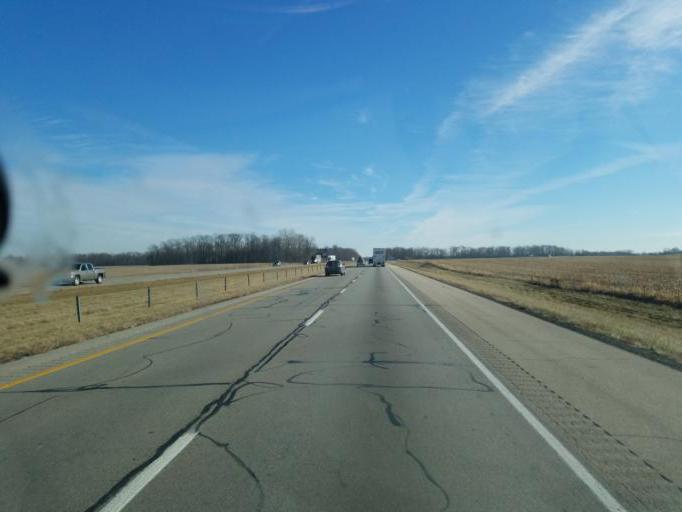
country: US
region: Indiana
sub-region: Henry County
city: New Castle
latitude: 39.8527
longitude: -85.3804
